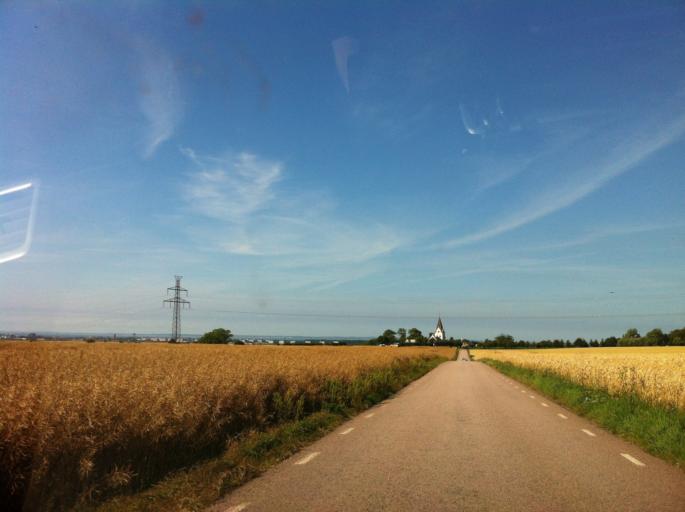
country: SE
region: Skane
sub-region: Landskrona
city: Asmundtorp
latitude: 55.9053
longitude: 12.9173
